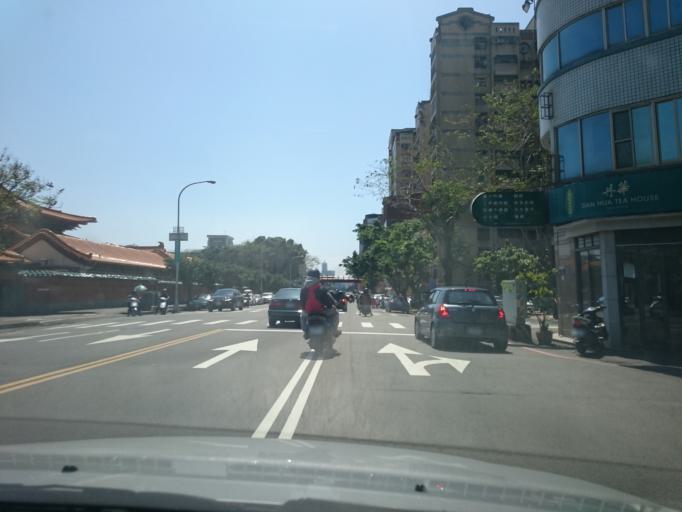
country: TW
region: Taiwan
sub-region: Taichung City
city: Taichung
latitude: 24.1551
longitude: 120.6897
